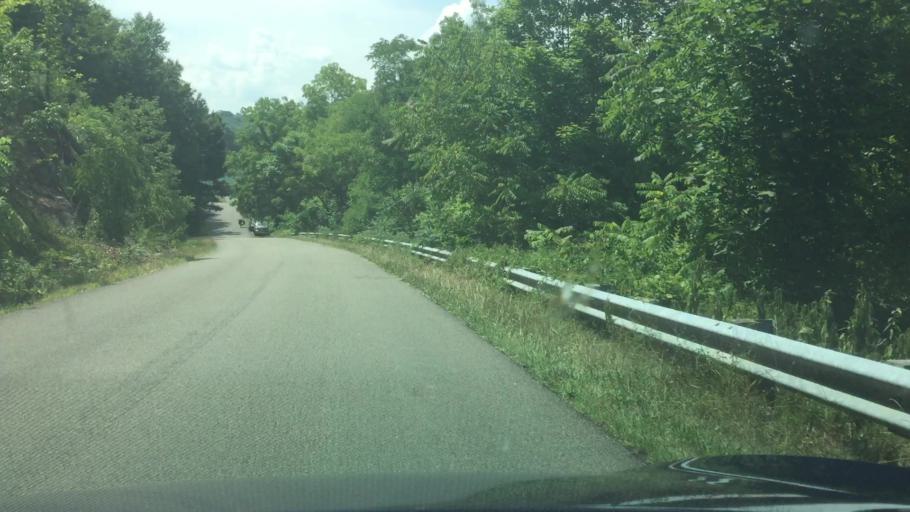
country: US
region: Virginia
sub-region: Wythe County
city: Wytheville
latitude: 36.9333
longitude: -81.0710
